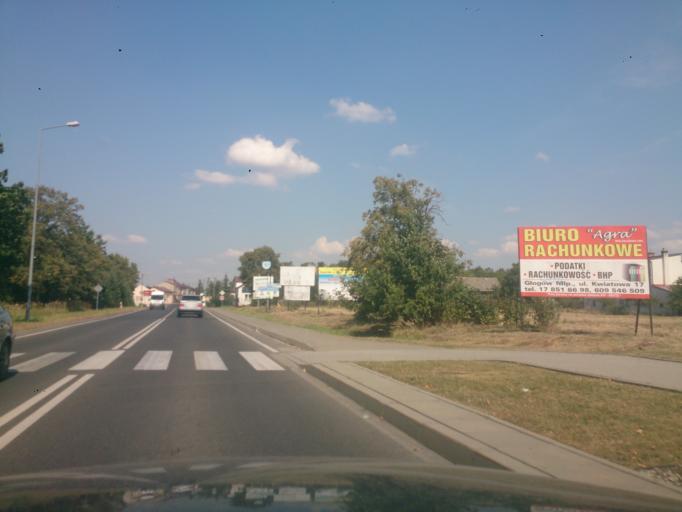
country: PL
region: Subcarpathian Voivodeship
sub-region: Powiat rzeszowski
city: Glogow Malopolski
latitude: 50.1458
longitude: 21.9631
